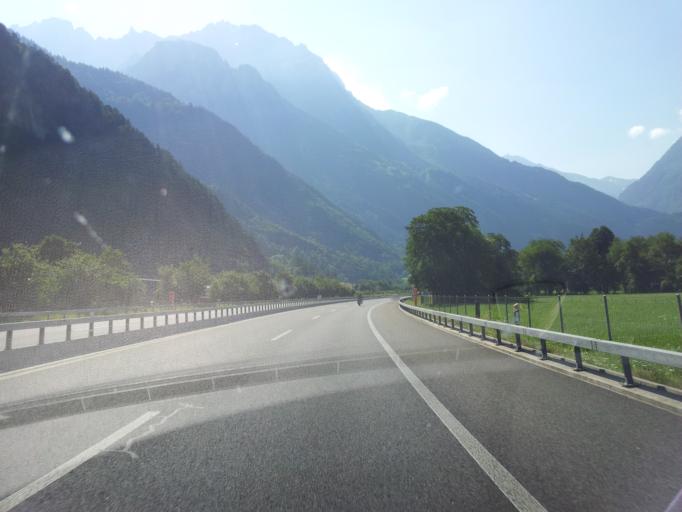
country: CH
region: Uri
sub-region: Uri
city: Erstfeld
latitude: 46.8146
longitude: 8.6532
